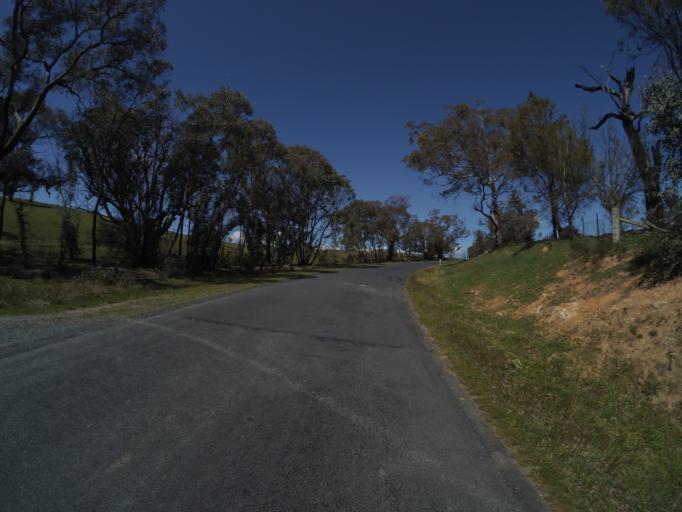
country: AU
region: New South Wales
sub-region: Yass Valley
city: Murrumbateman
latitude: -35.0921
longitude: 148.8503
